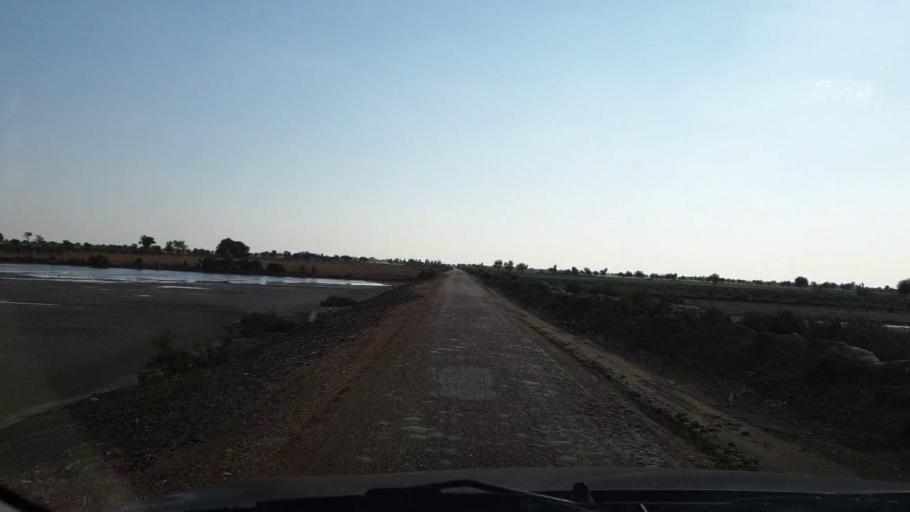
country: PK
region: Sindh
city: Sinjhoro
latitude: 26.0039
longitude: 68.8395
